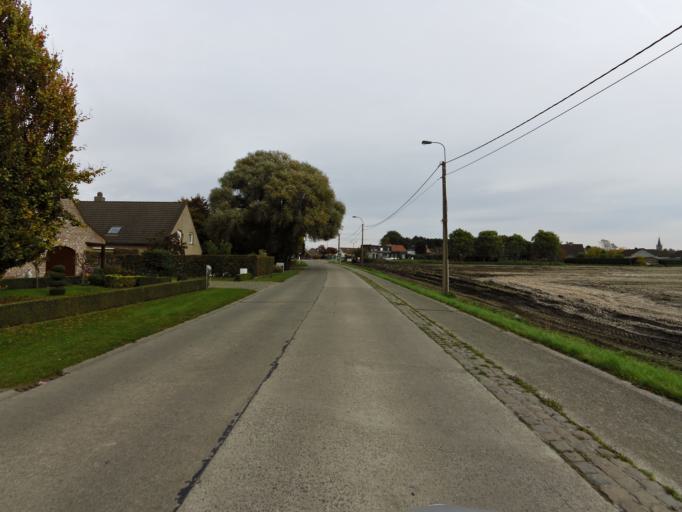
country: BE
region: Flanders
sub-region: Provincie West-Vlaanderen
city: Torhout
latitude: 51.1196
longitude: 3.0790
